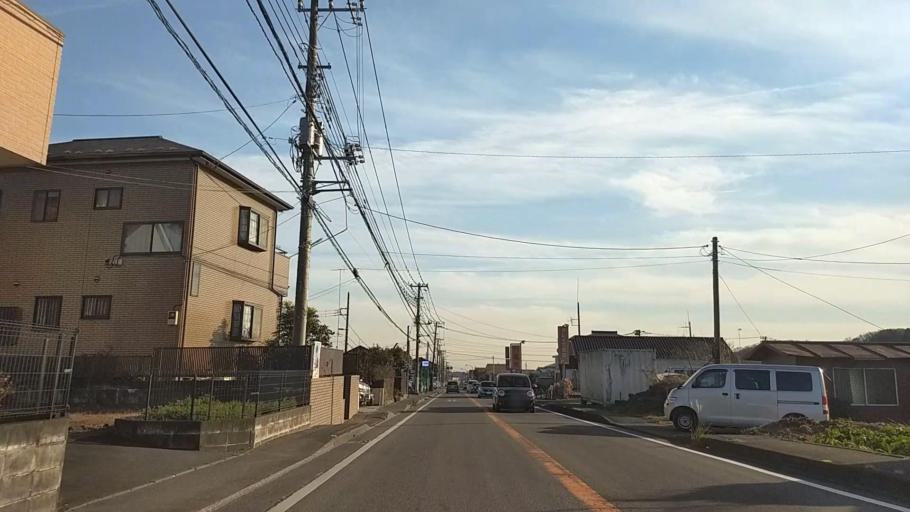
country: JP
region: Kanagawa
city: Zama
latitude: 35.5022
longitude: 139.3114
